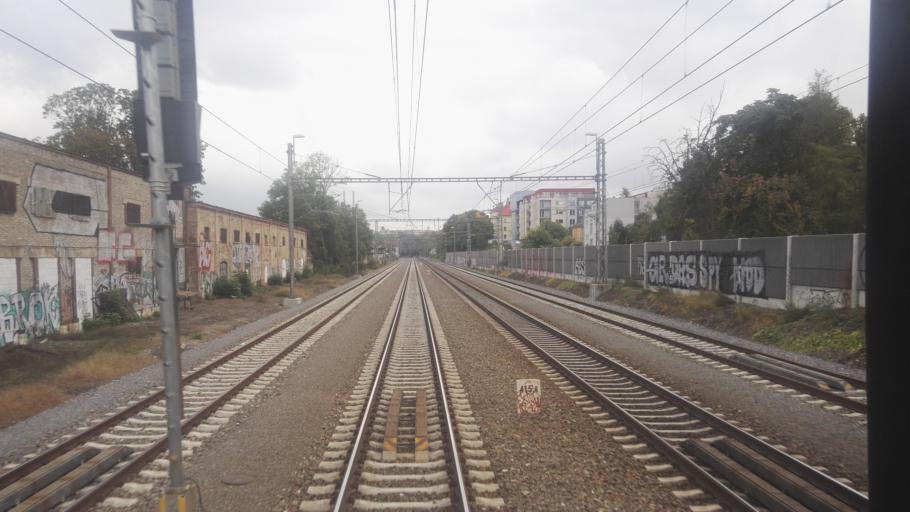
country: CZ
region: Praha
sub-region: Praha 1
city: Mala Strana
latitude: 50.1111
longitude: 14.3978
